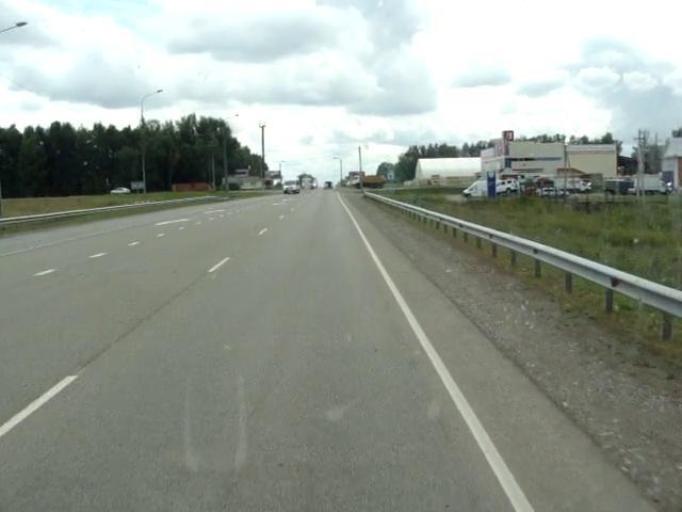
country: RU
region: Altai Krai
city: Zarya
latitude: 52.5762
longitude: 85.1795
